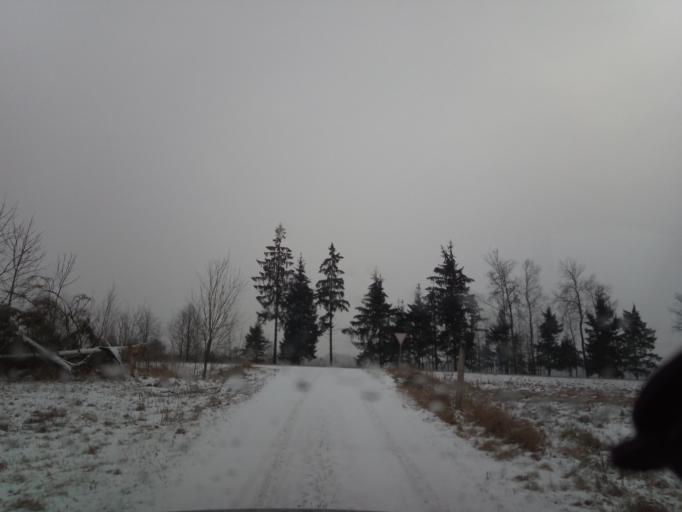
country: LT
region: Utenos apskritis
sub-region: Anyksciai
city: Anyksciai
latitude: 55.4017
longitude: 25.1699
